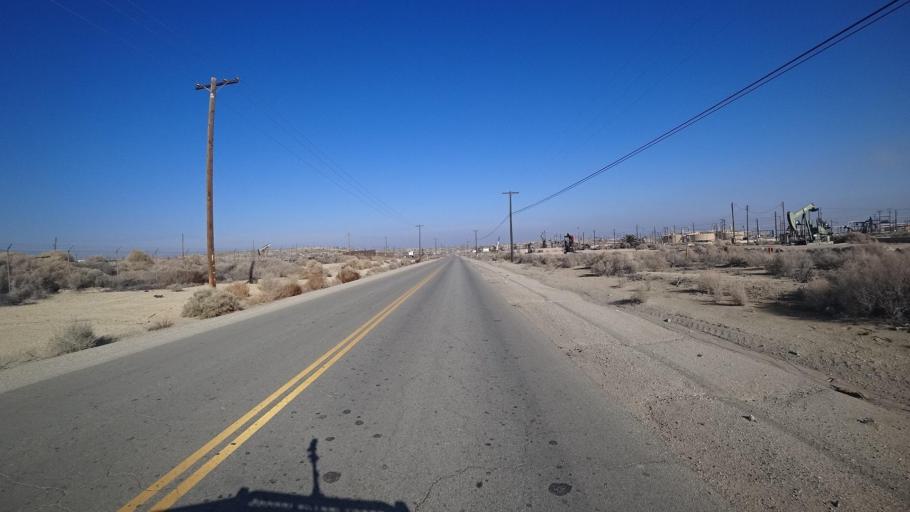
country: US
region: California
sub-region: Kern County
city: Taft Heights
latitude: 35.2130
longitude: -119.5982
